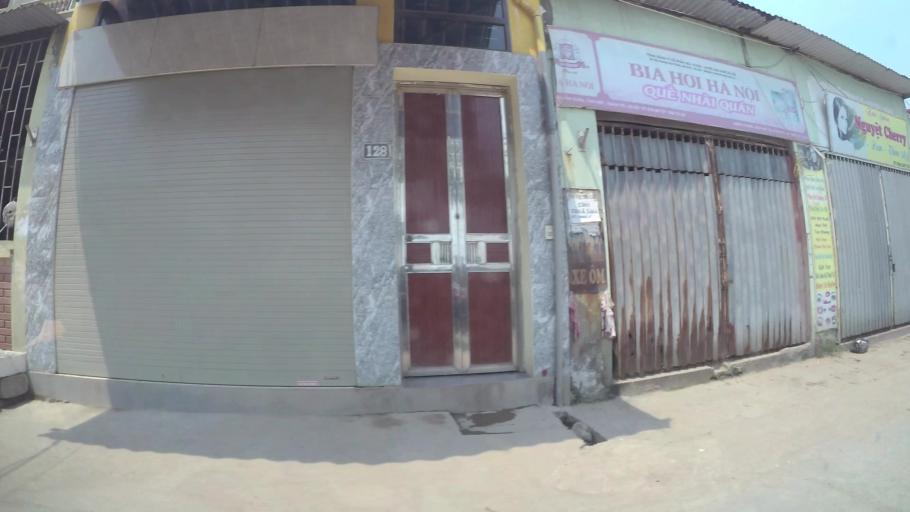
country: VN
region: Ha Noi
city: Van Dien
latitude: 20.9529
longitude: 105.8271
